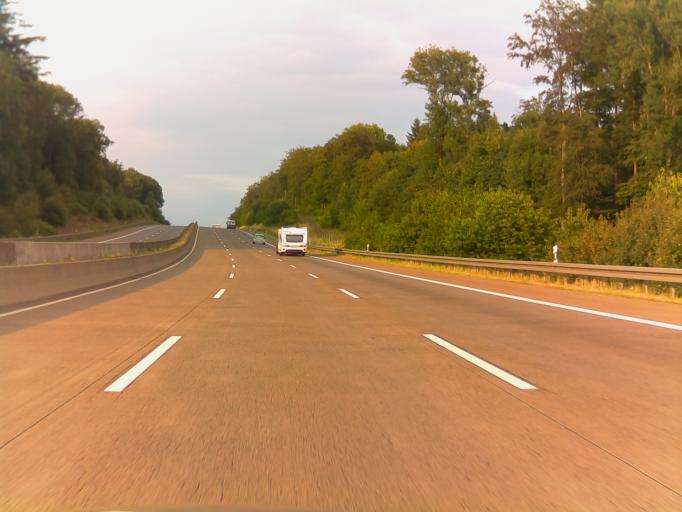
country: DE
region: Hesse
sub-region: Regierungsbezirk Giessen
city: Reiskirchen
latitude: 50.6133
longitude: 8.8700
